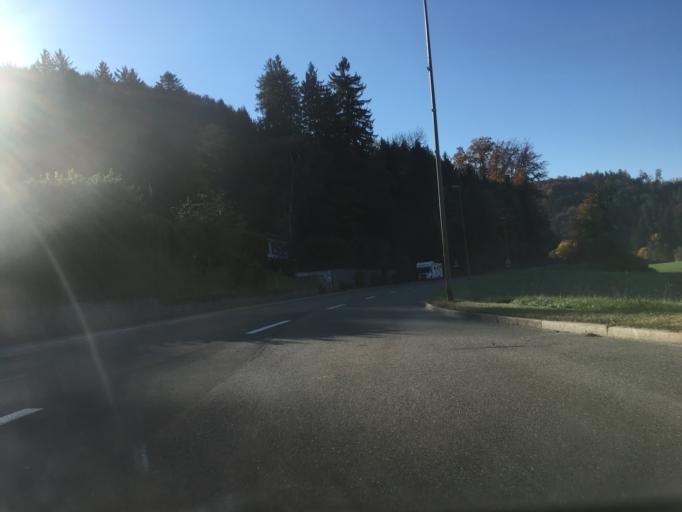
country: CH
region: Zurich
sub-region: Bezirk Affoltern
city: Wettswil / Ausser-Dorf
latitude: 47.3201
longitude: 8.4906
